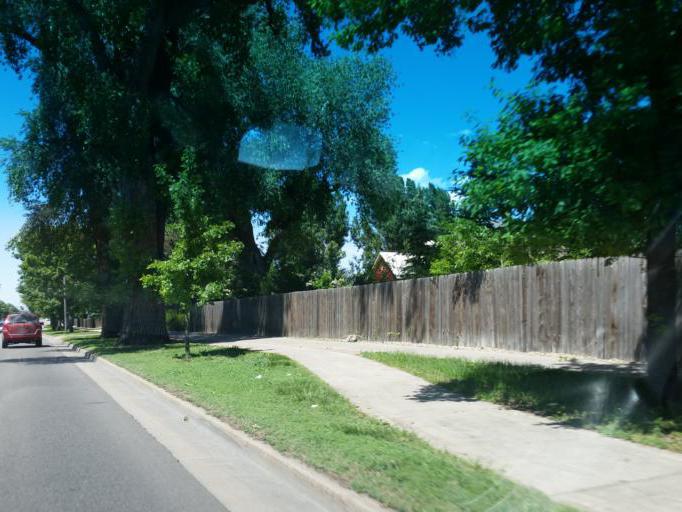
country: US
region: Colorado
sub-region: Larimer County
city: Fort Collins
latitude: 40.5426
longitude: -105.0961
